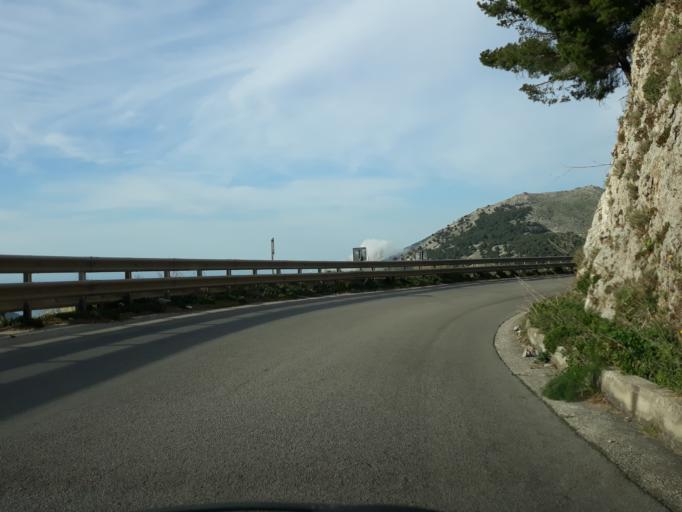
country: IT
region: Sicily
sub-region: Palermo
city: Torretta
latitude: 38.1191
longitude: 13.2426
